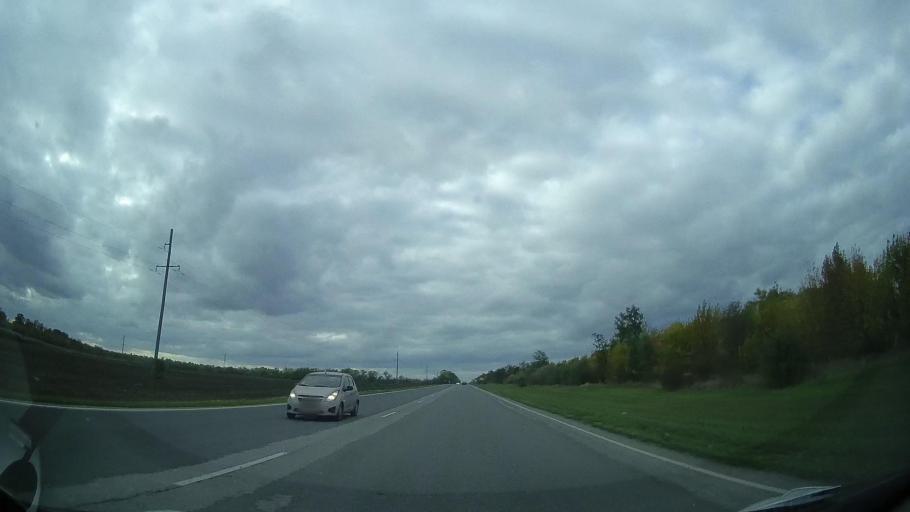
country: RU
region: Rostov
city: Mechetinskaya
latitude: 46.7944
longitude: 40.3838
